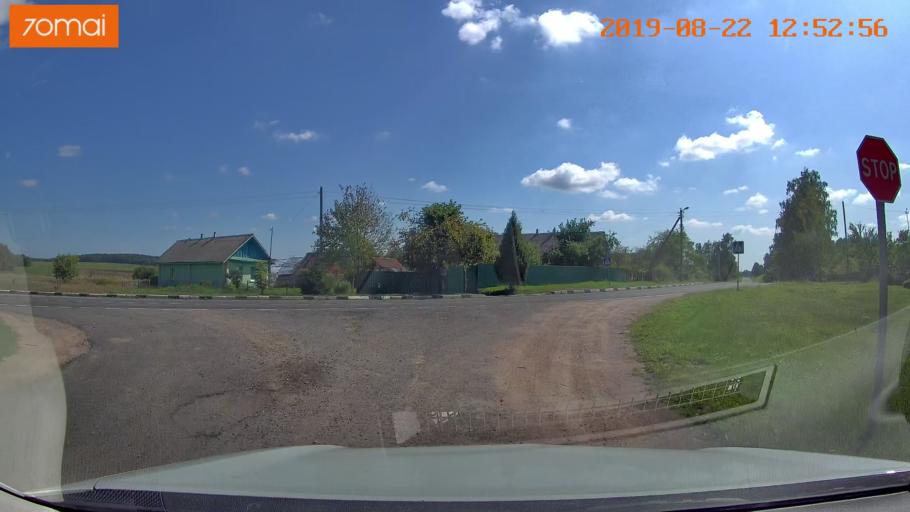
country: BY
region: Minsk
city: Prawdzinski
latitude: 53.4505
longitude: 27.6816
